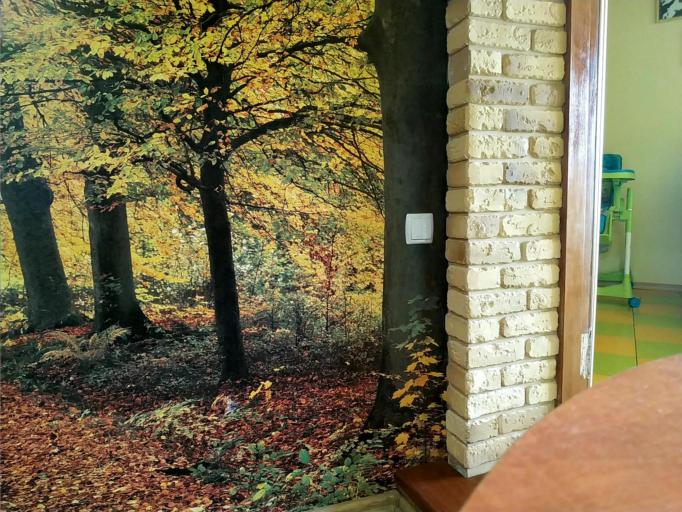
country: RU
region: Smolensk
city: Ozernyy
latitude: 55.4353
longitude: 32.7055
